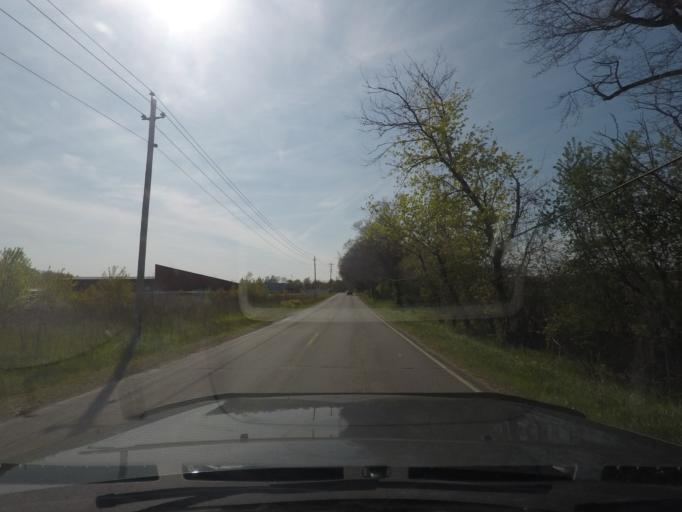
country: US
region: Indiana
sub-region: Elkhart County
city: Elkhart
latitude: 41.7043
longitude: -86.0075
